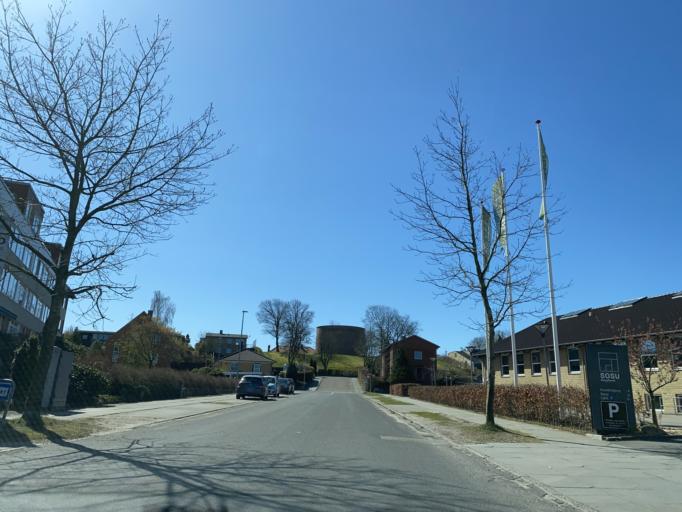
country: DK
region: Central Jutland
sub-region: Silkeborg Kommune
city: Silkeborg
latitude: 56.1685
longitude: 9.5616
